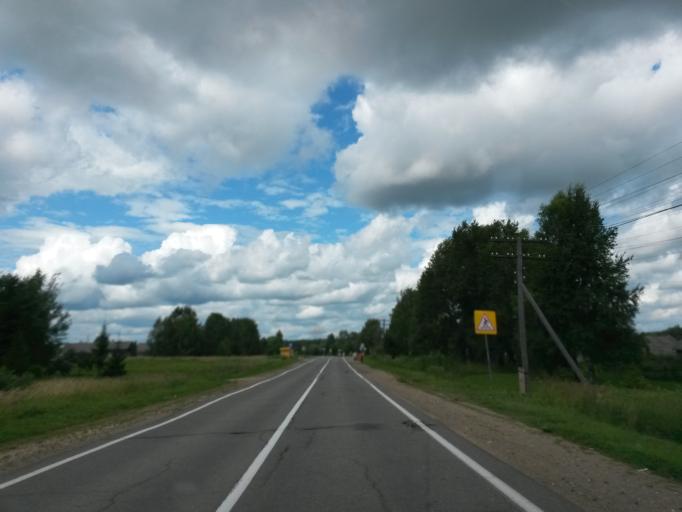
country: RU
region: Jaroslavl
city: Tutayev
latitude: 57.9365
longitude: 39.5003
